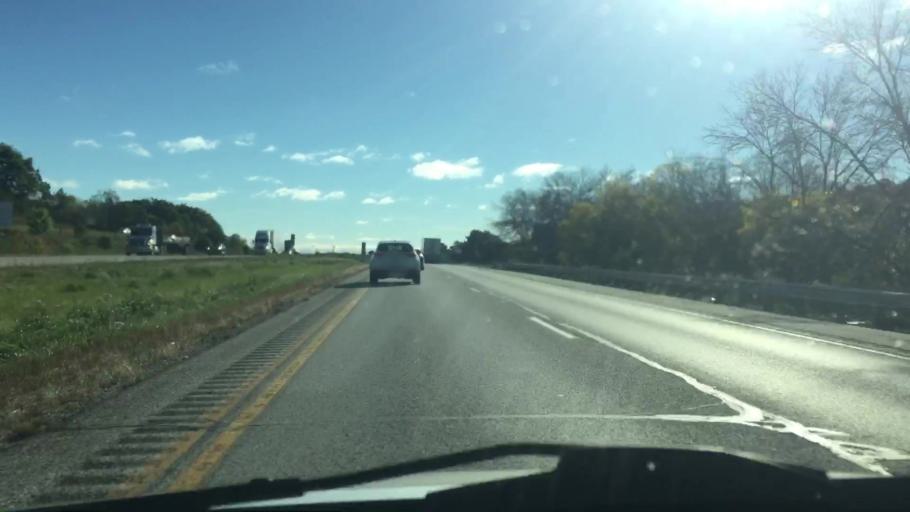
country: US
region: Wisconsin
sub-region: Waukesha County
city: Delafield
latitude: 43.0497
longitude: -88.3580
